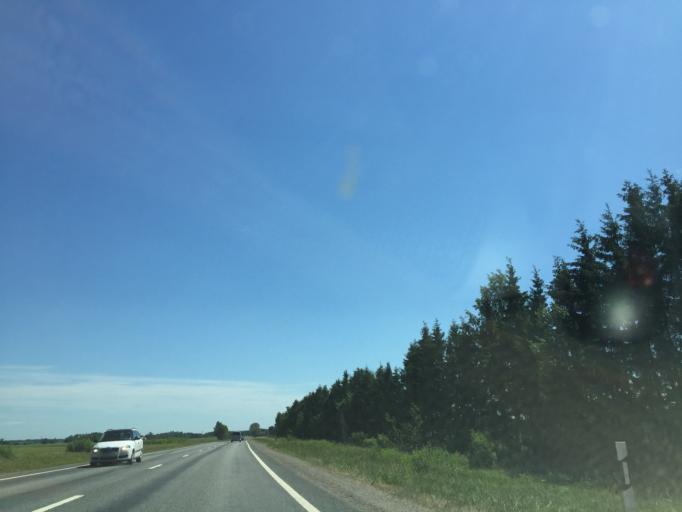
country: LV
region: Jaunpils
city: Jaunpils
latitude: 56.6640
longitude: 22.9164
